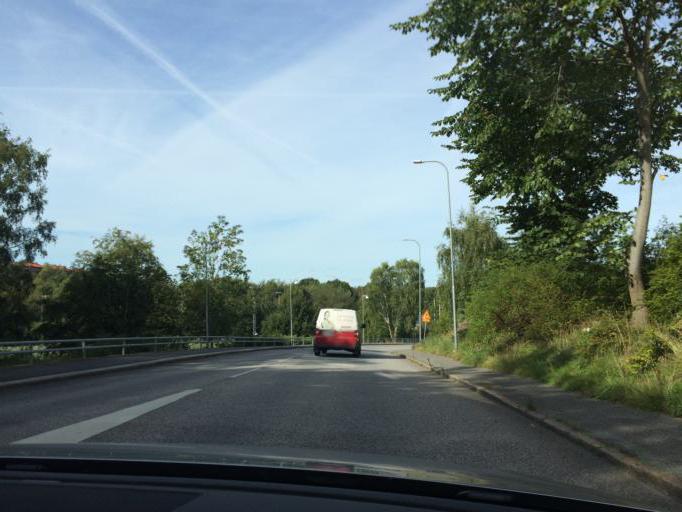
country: SE
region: Vaestra Goetaland
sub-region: Goteborg
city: Goeteborg
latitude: 57.6801
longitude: 11.9843
